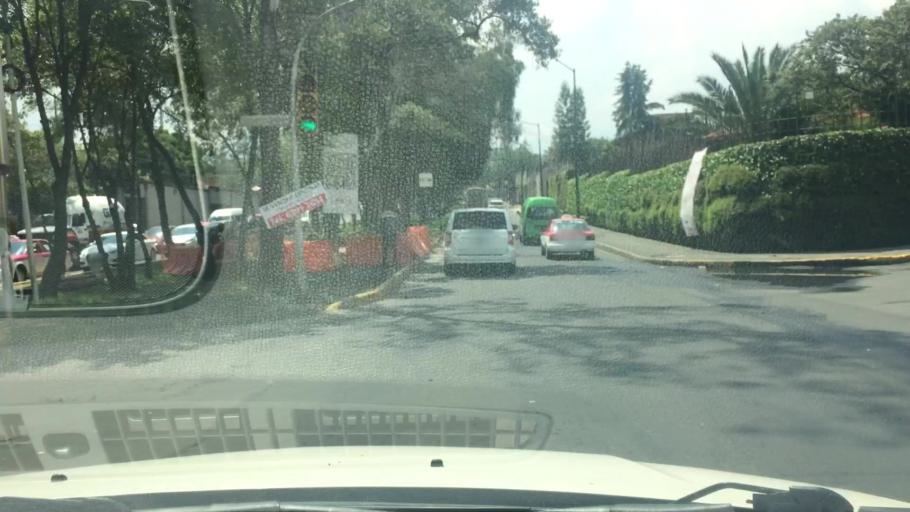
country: MX
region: Mexico City
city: Magdalena Contreras
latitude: 19.3091
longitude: -99.2045
